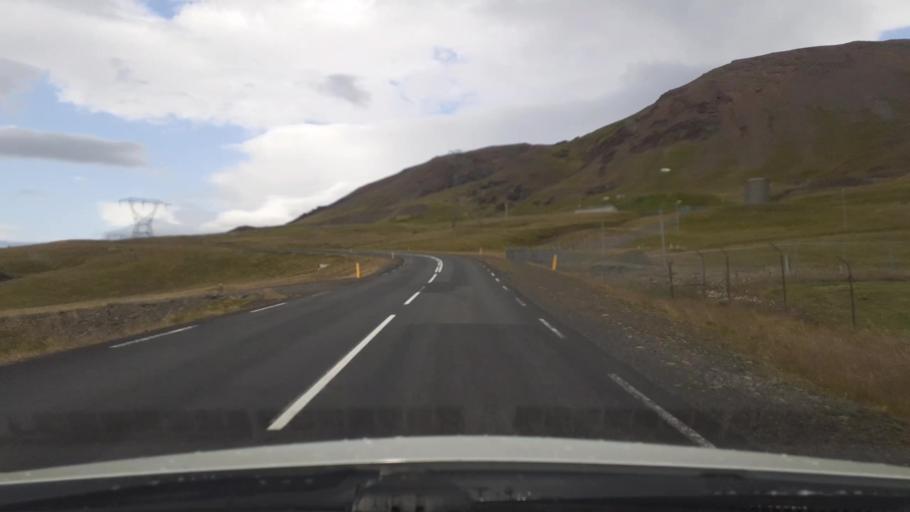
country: IS
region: Capital Region
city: Mosfellsbaer
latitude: 64.3983
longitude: -21.4643
